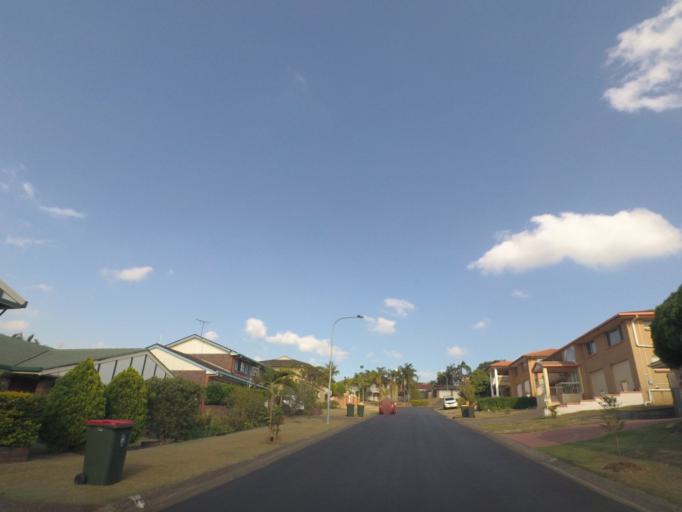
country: AU
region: Queensland
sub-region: Brisbane
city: Robertson
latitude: -27.5620
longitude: 153.0576
